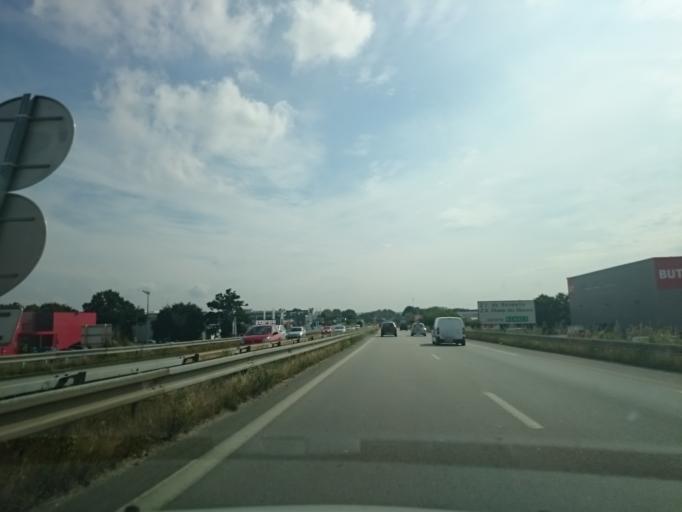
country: FR
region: Brittany
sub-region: Departement du Morbihan
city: Vannes
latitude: 47.6637
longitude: -2.7878
